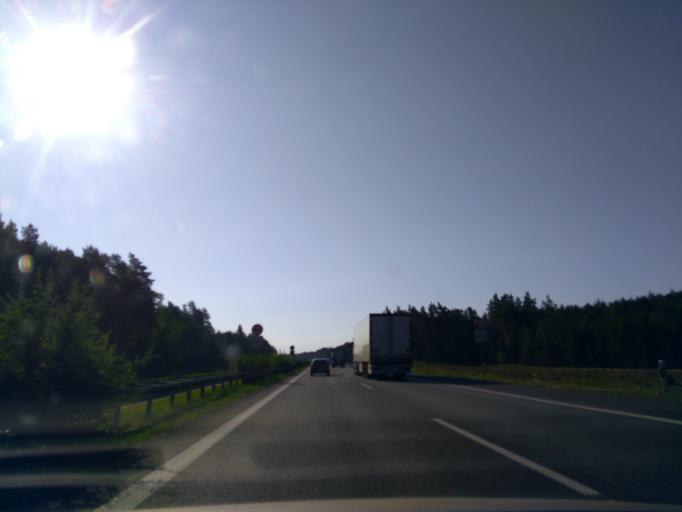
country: DE
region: Brandenburg
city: Birkenwerder
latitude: 52.6878
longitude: 13.3275
